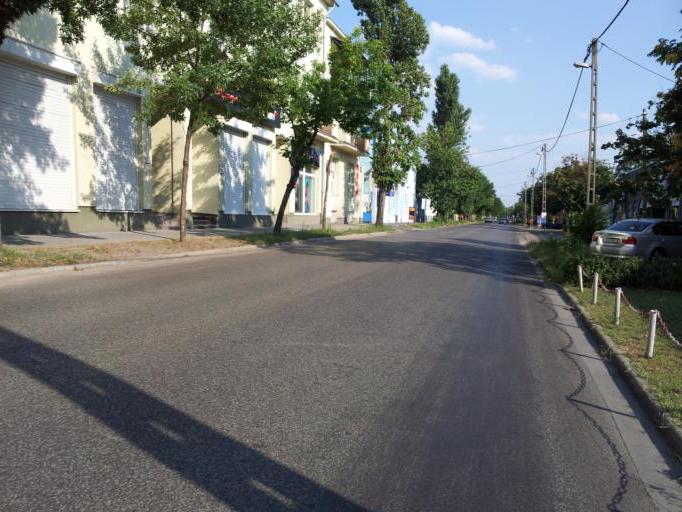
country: HU
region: Budapest
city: Budapest X. keruelet
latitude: 47.4806
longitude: 19.1223
